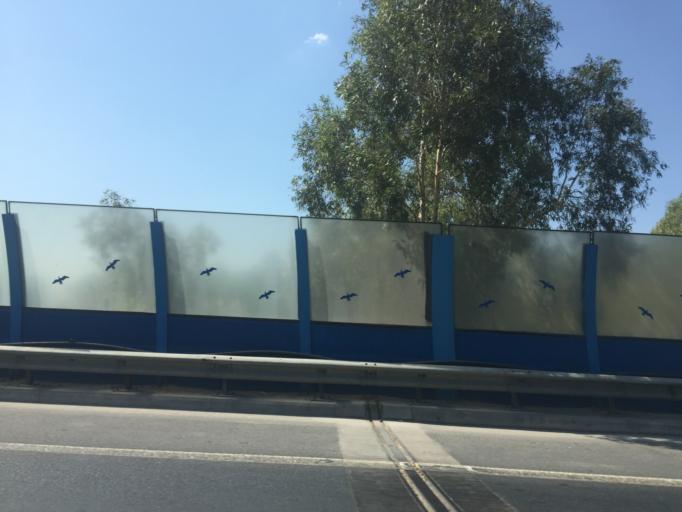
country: TR
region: Izmir
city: Karsiyaka
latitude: 38.4837
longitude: 27.1434
